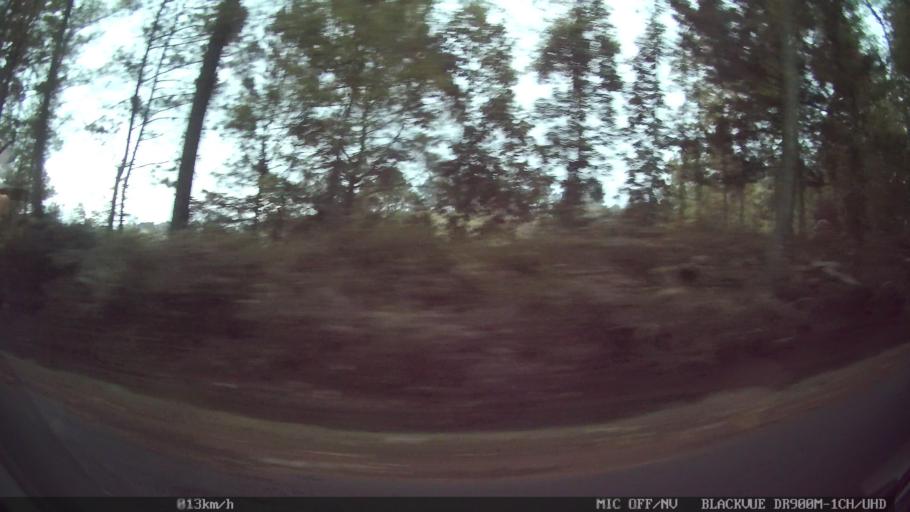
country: ID
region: Bali
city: Banjar Kedisan
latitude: -8.2638
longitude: 115.3335
